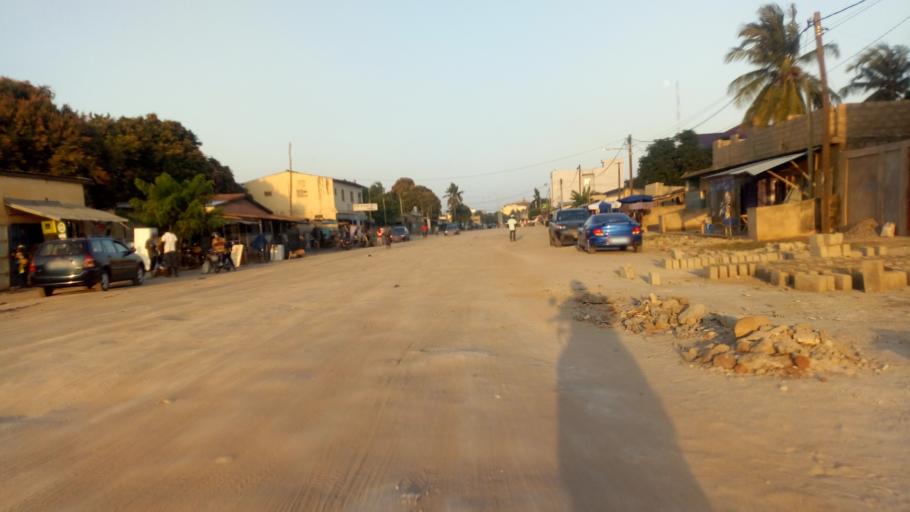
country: TG
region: Maritime
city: Lome
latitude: 6.1929
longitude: 1.1994
